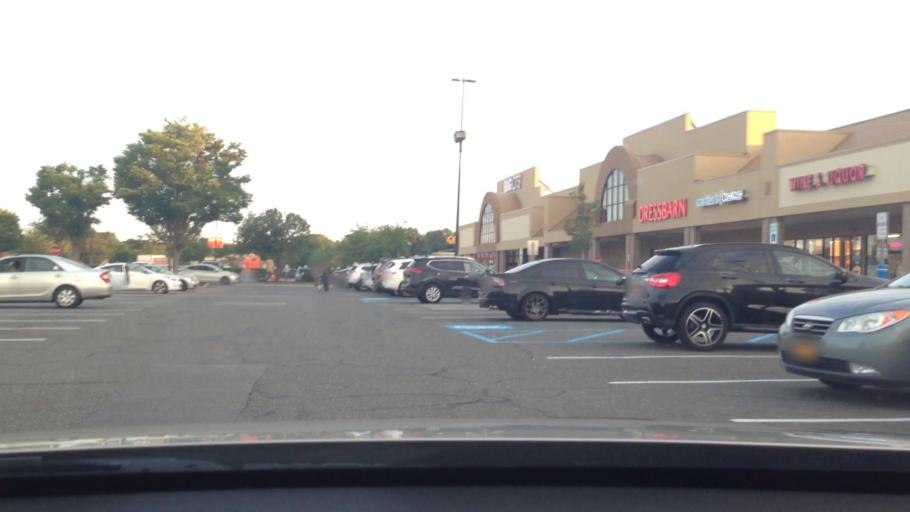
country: US
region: New York
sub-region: Suffolk County
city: Centereach
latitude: 40.8620
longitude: -73.0823
